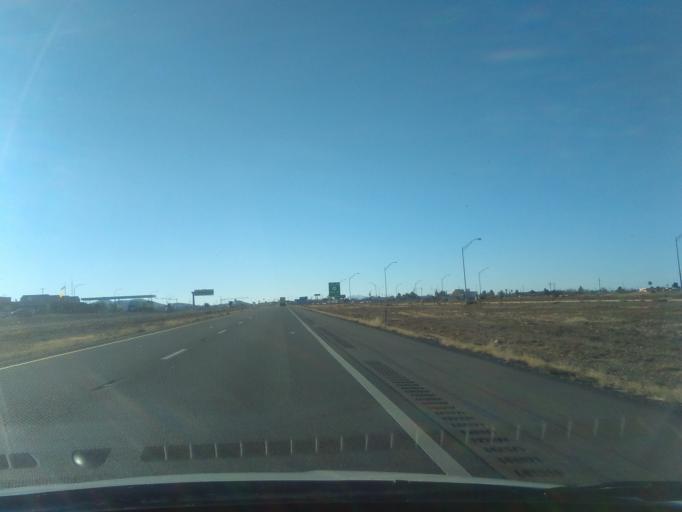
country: US
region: New Mexico
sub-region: Hidalgo County
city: Lordsburg
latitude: 32.3414
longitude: -108.6945
